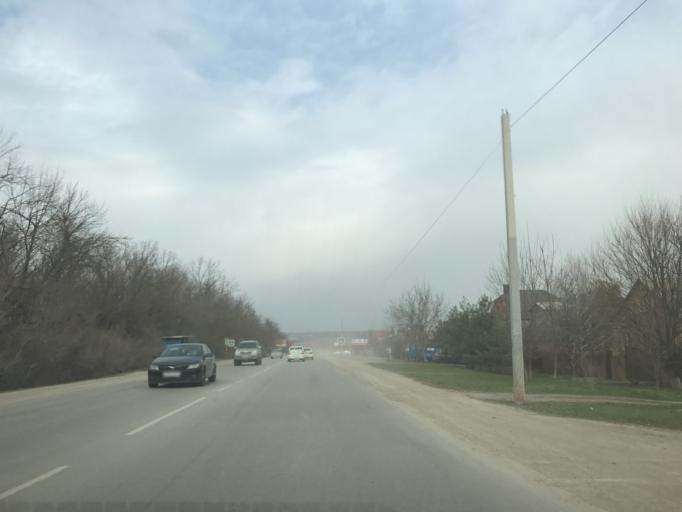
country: RU
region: Rostov
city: Aksay
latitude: 47.2826
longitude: 39.9010
